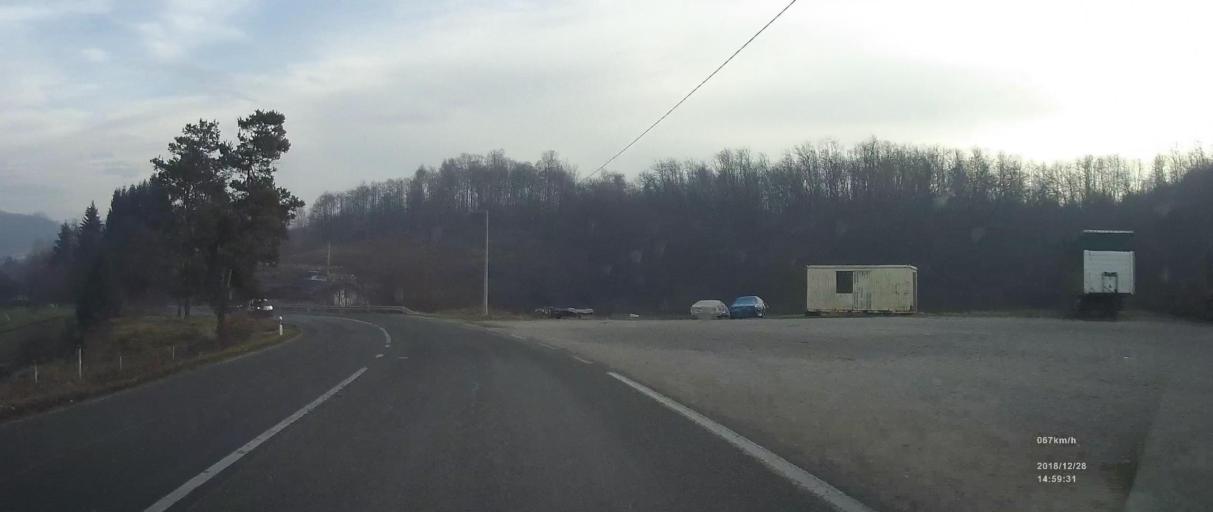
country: HR
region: Karlovacka
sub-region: Grad Karlovac
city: Karlovac
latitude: 45.4574
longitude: 15.4831
